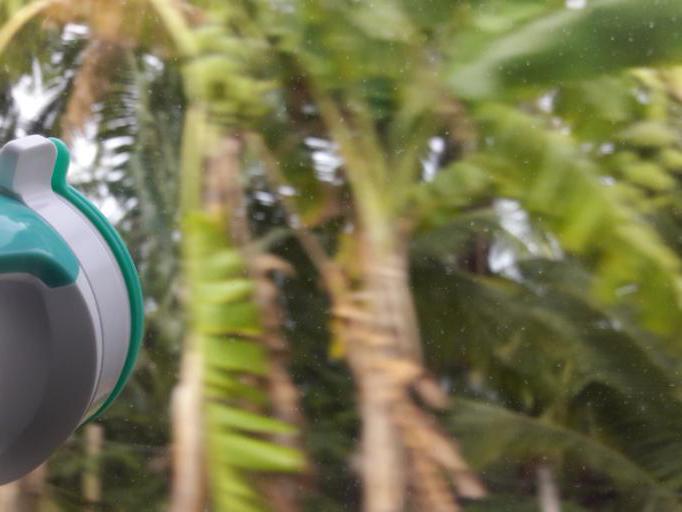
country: TH
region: Ratchaburi
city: Damnoen Saduak
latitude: 13.5361
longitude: 99.9954
